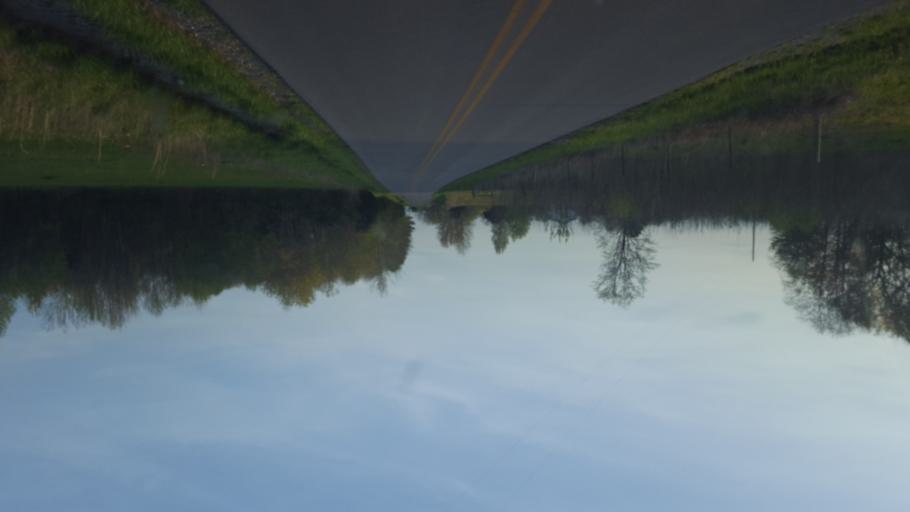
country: US
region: Kentucky
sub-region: Metcalfe County
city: Edmonton
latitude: 37.0120
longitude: -85.7236
